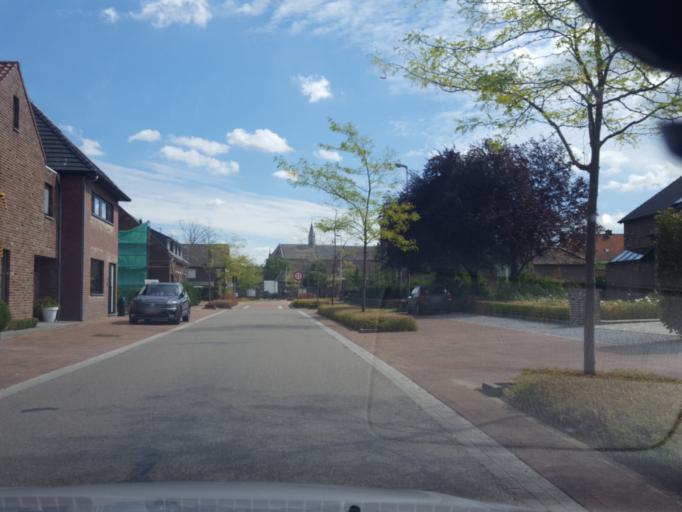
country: BE
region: Flanders
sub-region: Provincie Limburg
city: Maasmechelen
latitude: 50.9249
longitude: 5.6970
